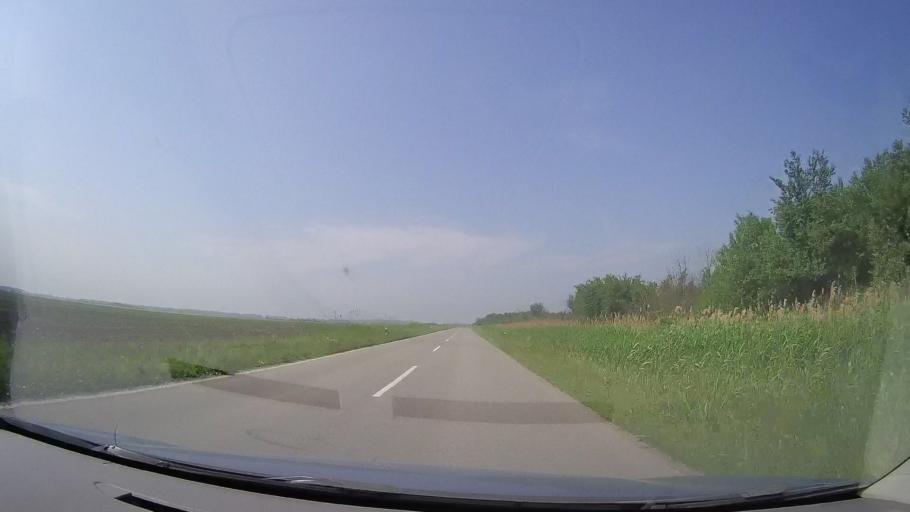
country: RS
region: Autonomna Pokrajina Vojvodina
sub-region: Srednjebanatski Okrug
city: Secanj
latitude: 45.3949
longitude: 20.8072
